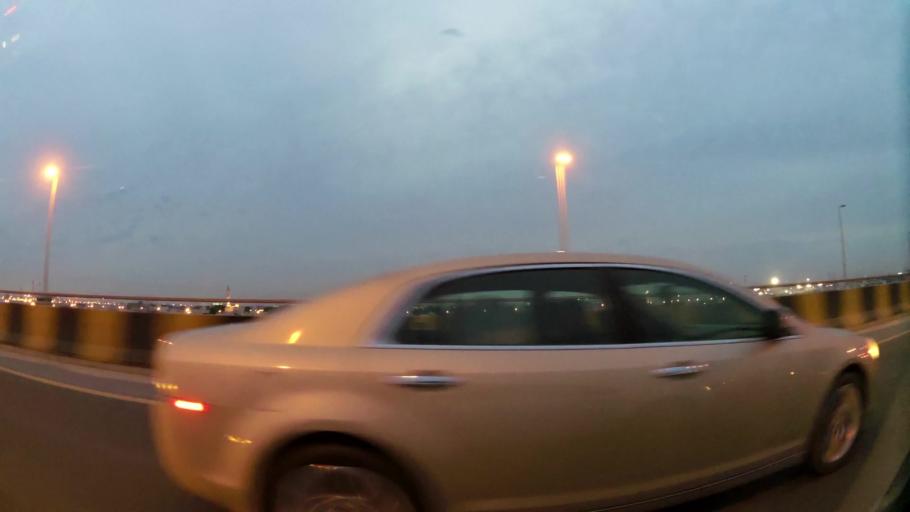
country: BH
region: Northern
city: Madinat `Isa
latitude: 26.1723
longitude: 50.5419
